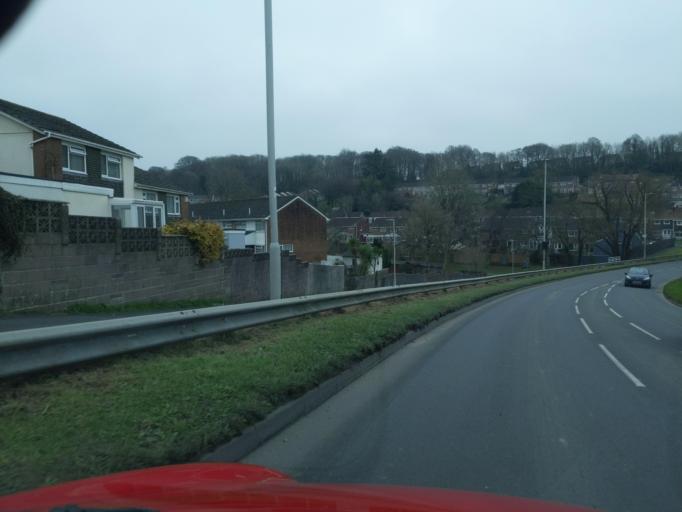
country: GB
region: England
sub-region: Devon
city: Plympton
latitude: 50.3871
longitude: -4.0350
